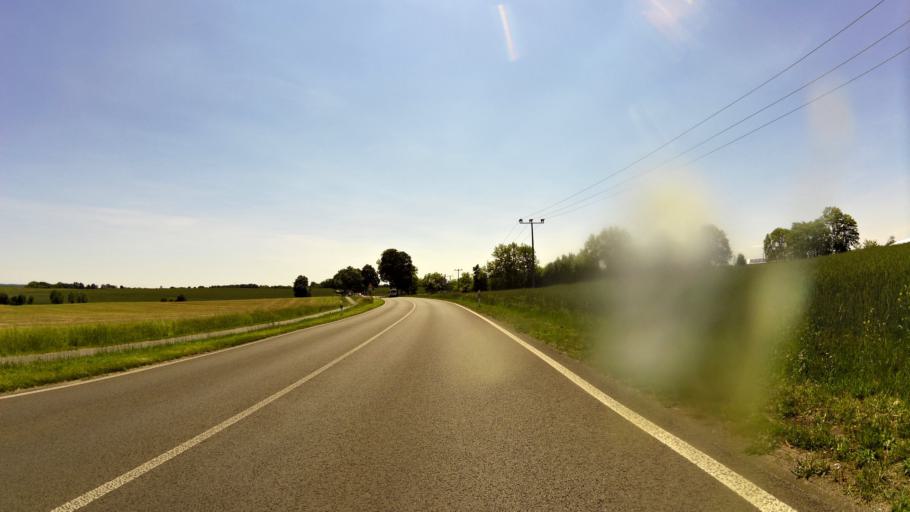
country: DE
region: Brandenburg
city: Lebus
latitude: 52.4008
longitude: 14.5176
